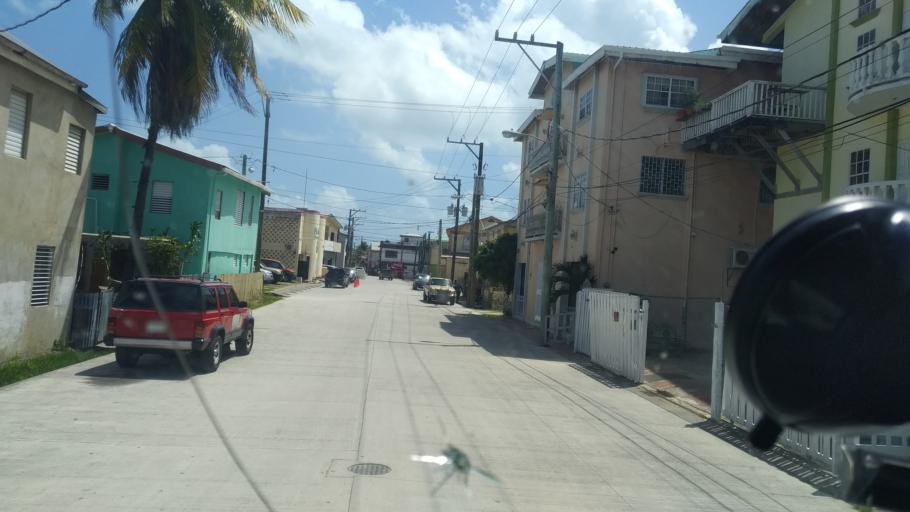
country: BZ
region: Belize
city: Belize City
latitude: 17.4916
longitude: -88.1917
